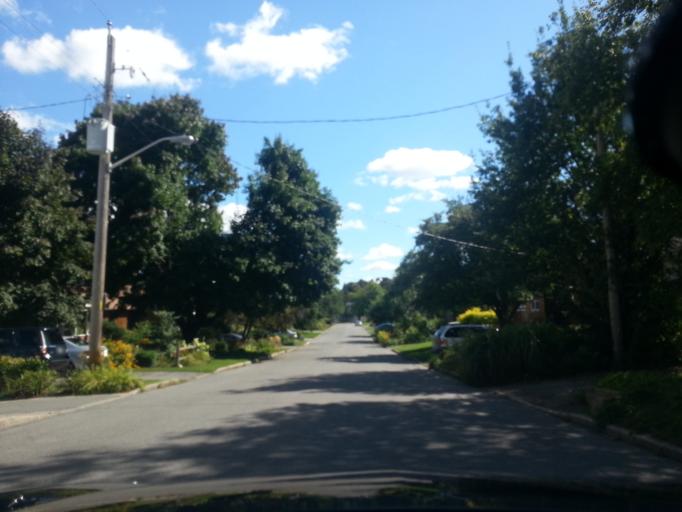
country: CA
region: Ontario
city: Ottawa
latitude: 45.3817
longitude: -75.7560
